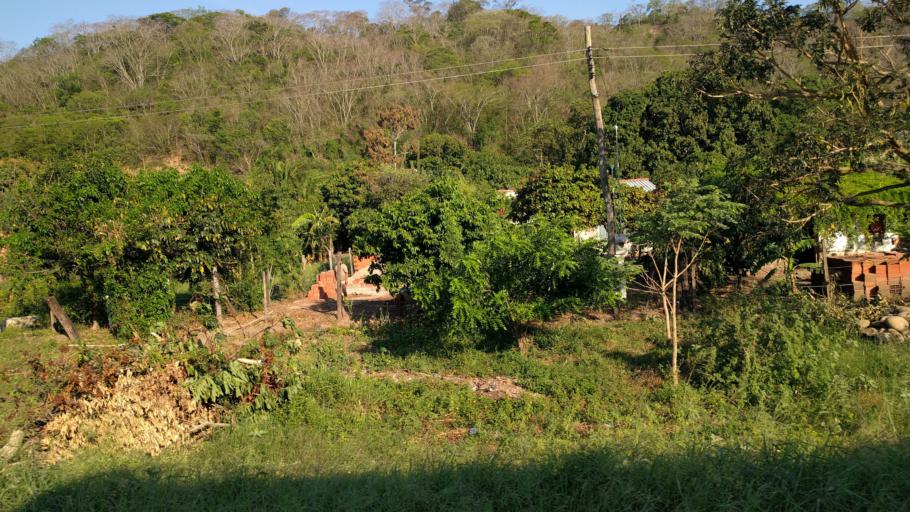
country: BO
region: Santa Cruz
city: Jorochito
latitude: -18.0713
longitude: -63.4412
